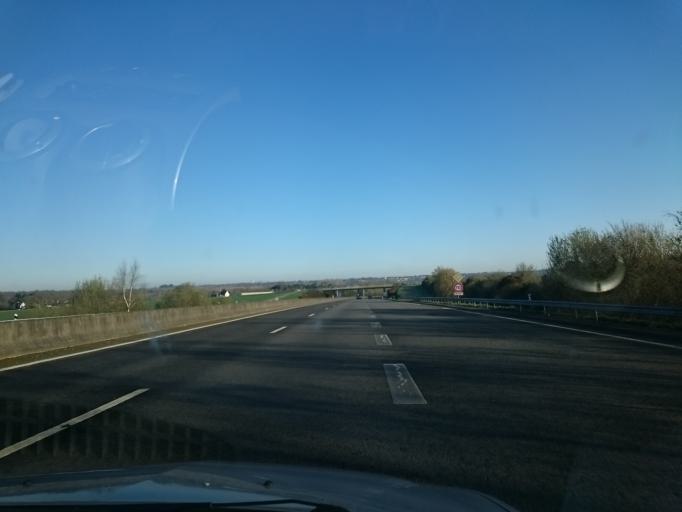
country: FR
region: Brittany
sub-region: Departement d'Ille-et-Vilaine
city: Cesson-Sevigne
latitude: 48.1224
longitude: -1.5732
